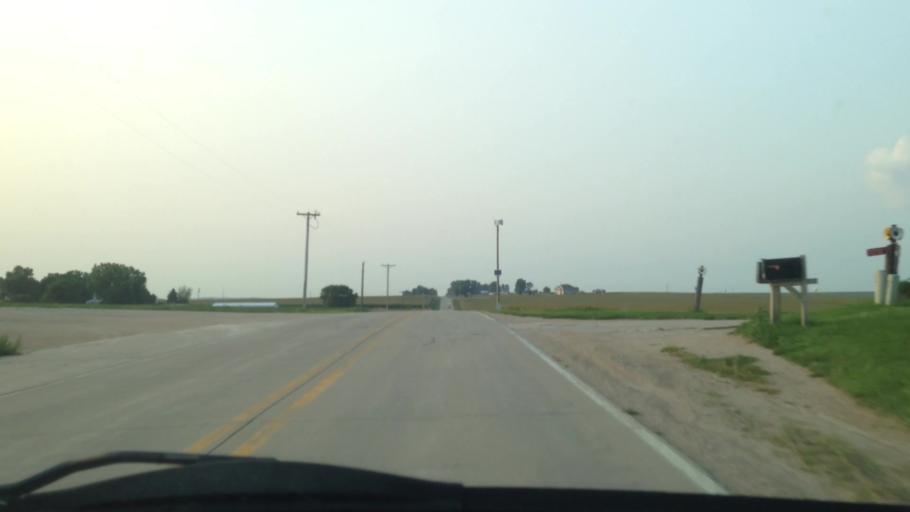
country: US
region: Iowa
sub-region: Benton County
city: Atkins
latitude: 41.9695
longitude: -91.8727
